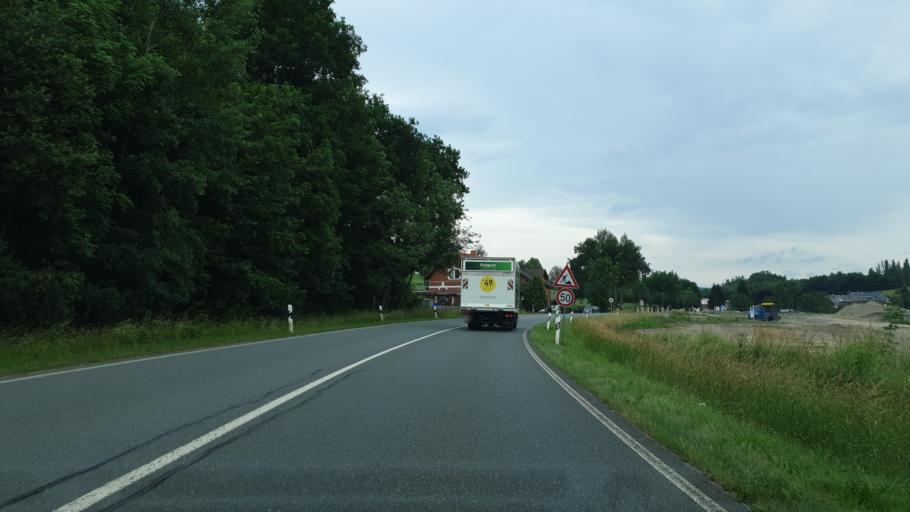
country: DE
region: Saxony
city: Rodewisch
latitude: 50.5457
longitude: 12.3903
